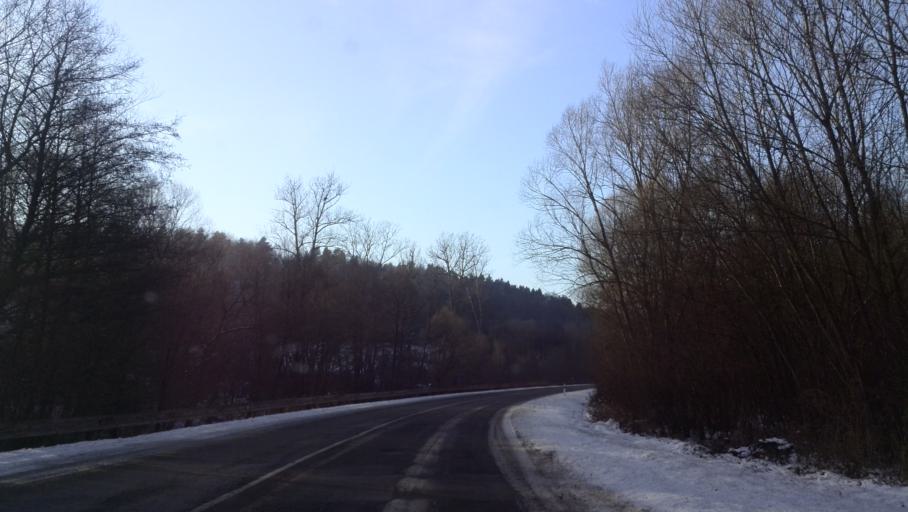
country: SK
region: Presovsky
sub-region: Okres Presov
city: Presov
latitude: 48.9591
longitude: 21.1164
